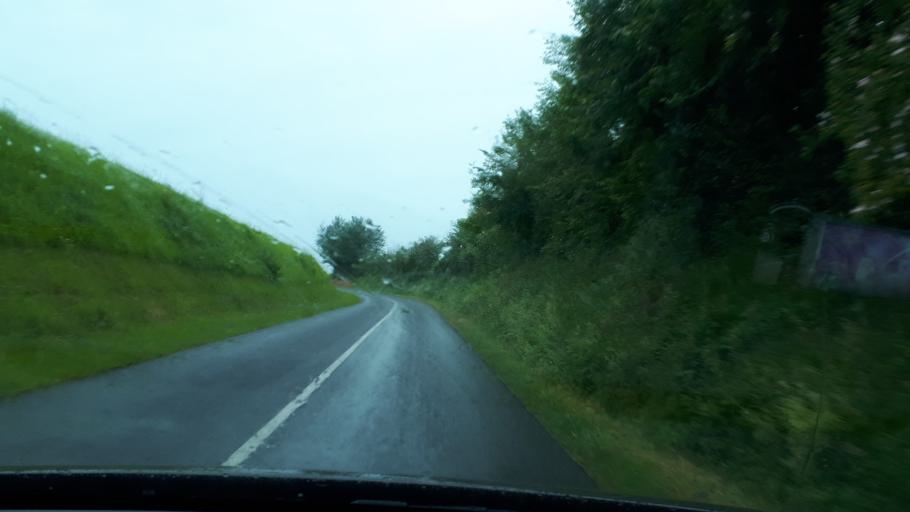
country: FR
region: Centre
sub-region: Departement du Loir-et-Cher
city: Lunay
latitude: 47.8067
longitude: 0.9119
